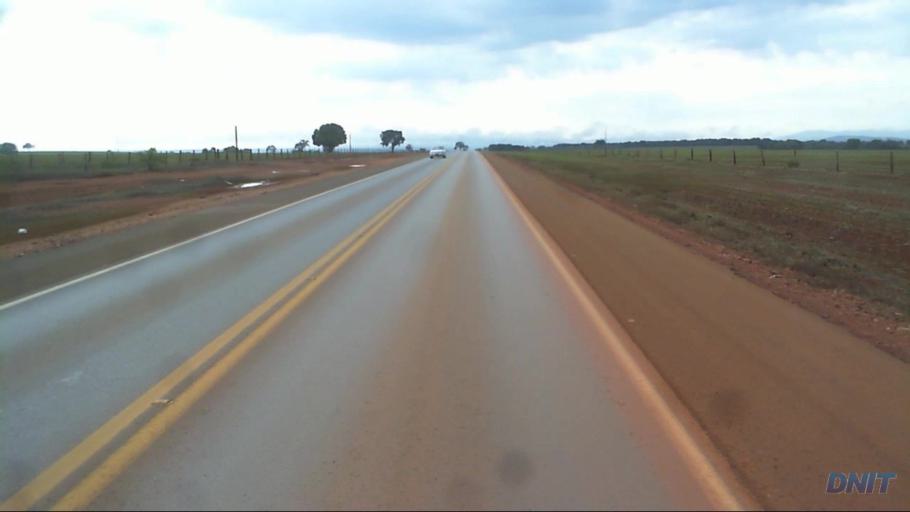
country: BR
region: Goias
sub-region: Uruacu
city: Uruacu
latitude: -14.6931
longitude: -49.1251
